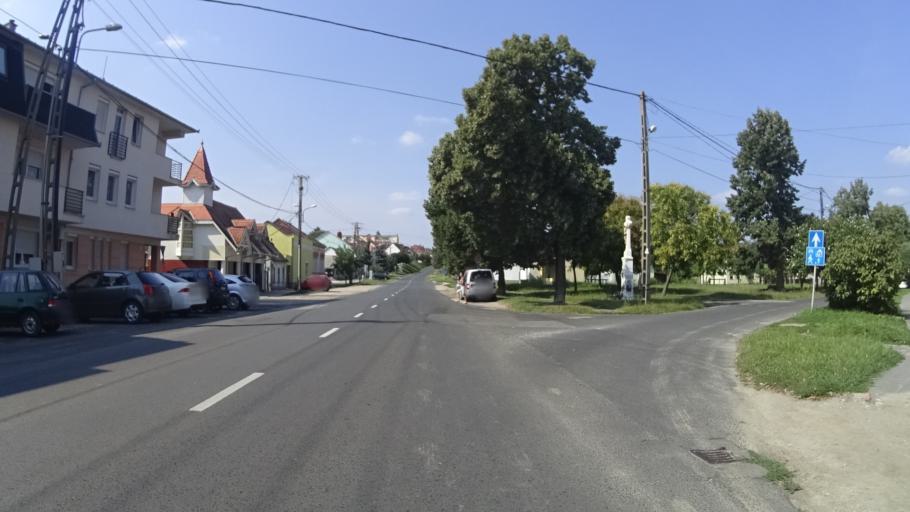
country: HU
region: Zala
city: Nagykanizsa
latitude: 46.4589
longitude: 16.9992
